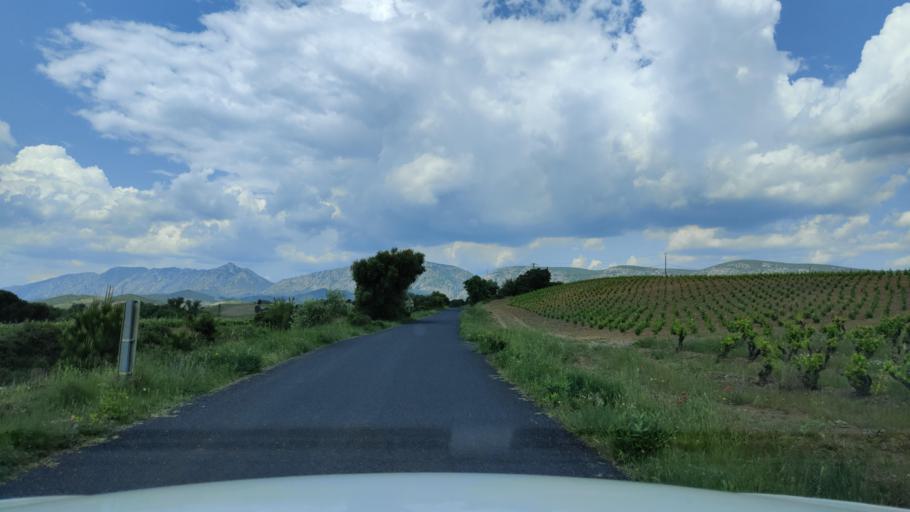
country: FR
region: Languedoc-Roussillon
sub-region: Departement des Pyrenees-Orientales
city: Estagel
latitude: 42.7952
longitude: 2.6745
